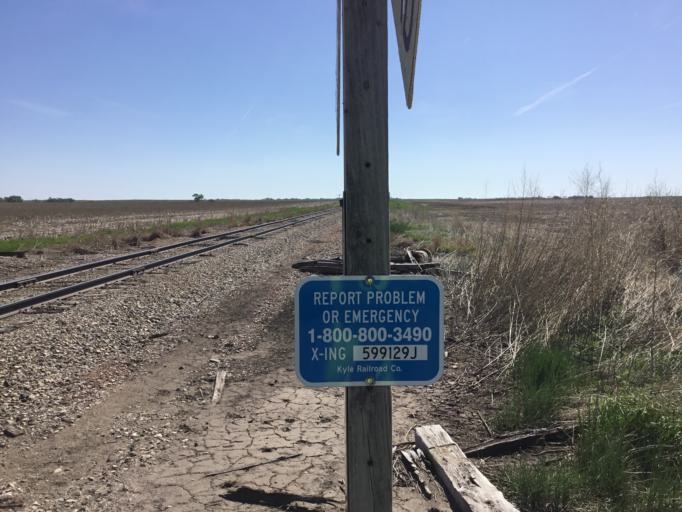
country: US
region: Kansas
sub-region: Smith County
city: Smith Center
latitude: 39.7633
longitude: -98.9541
